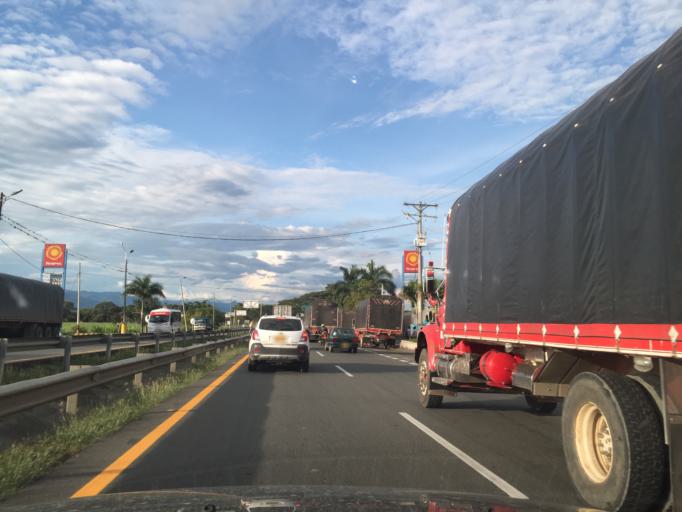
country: CO
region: Valle del Cauca
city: Andalucia
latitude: 4.1616
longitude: -76.1758
